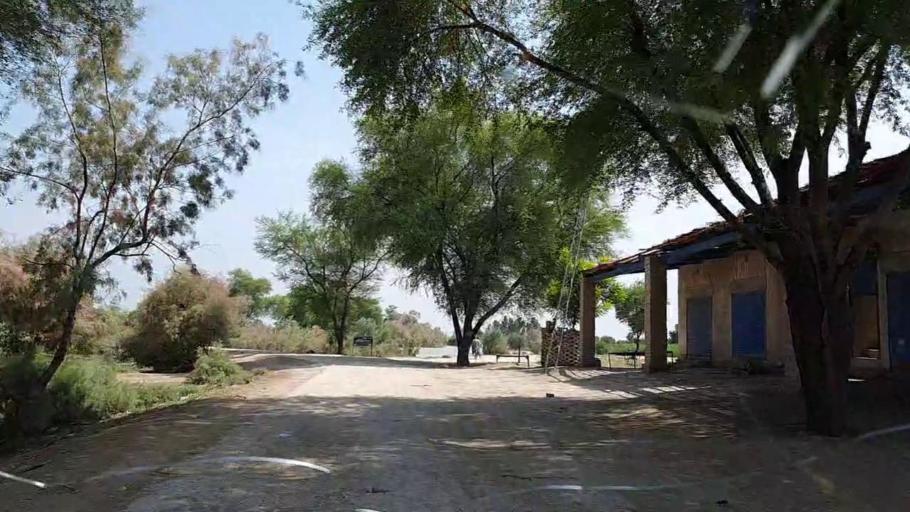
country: PK
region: Sindh
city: Khanpur
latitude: 27.8168
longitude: 69.3059
